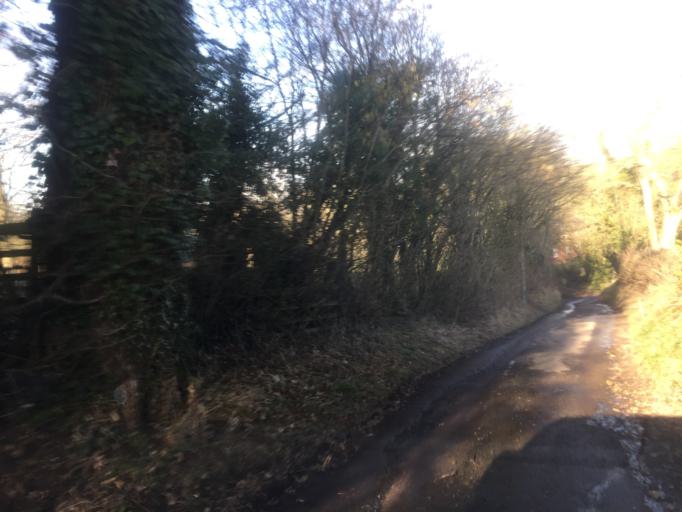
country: GB
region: England
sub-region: Shropshire
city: Much Wenlock
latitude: 52.5287
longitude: -2.5080
